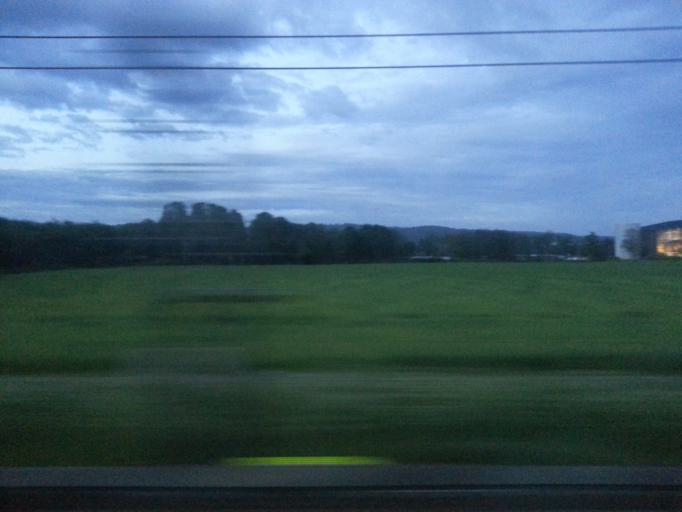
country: NO
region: Akershus
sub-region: Skedsmo
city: Lillestrom
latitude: 59.9733
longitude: 11.0698
